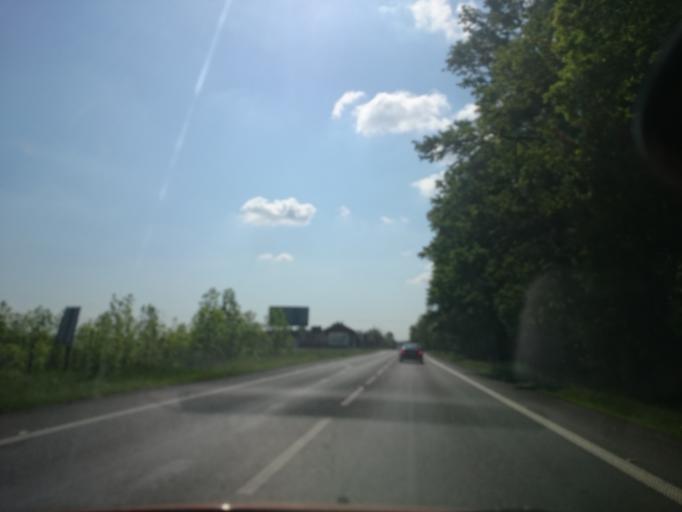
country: PL
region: Opole Voivodeship
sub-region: Powiat opolski
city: Naklo
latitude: 50.5878
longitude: 18.1024
